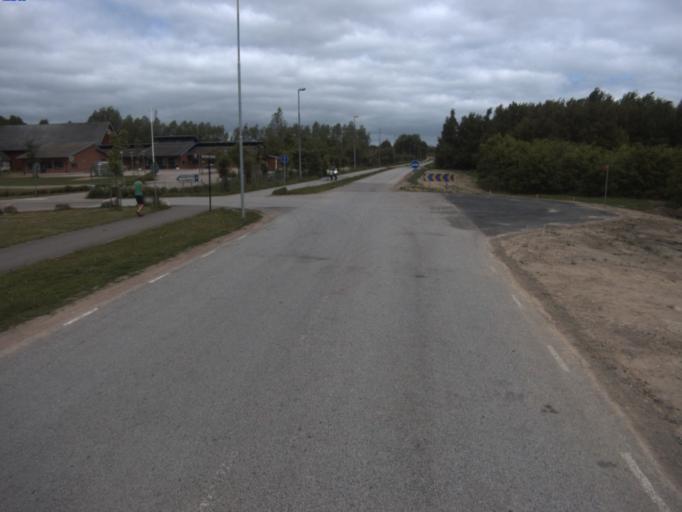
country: SE
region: Skane
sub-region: Helsingborg
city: Helsingborg
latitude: 56.0554
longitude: 12.7351
